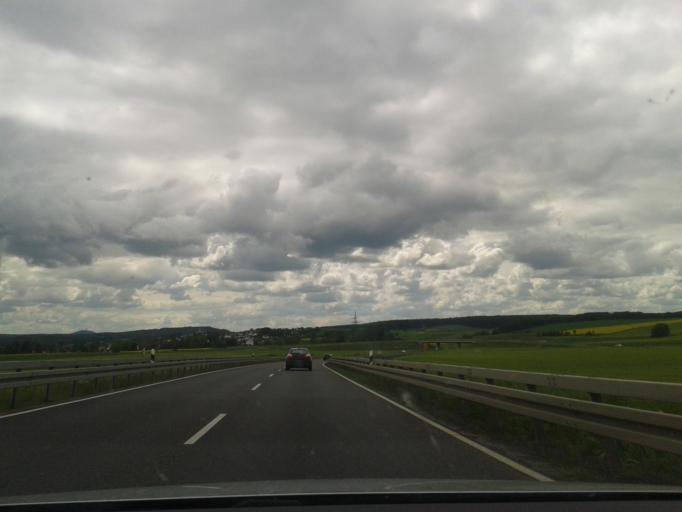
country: DE
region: Hesse
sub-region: Regierungsbezirk Giessen
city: Fronhausen
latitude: 50.7537
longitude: 8.7291
